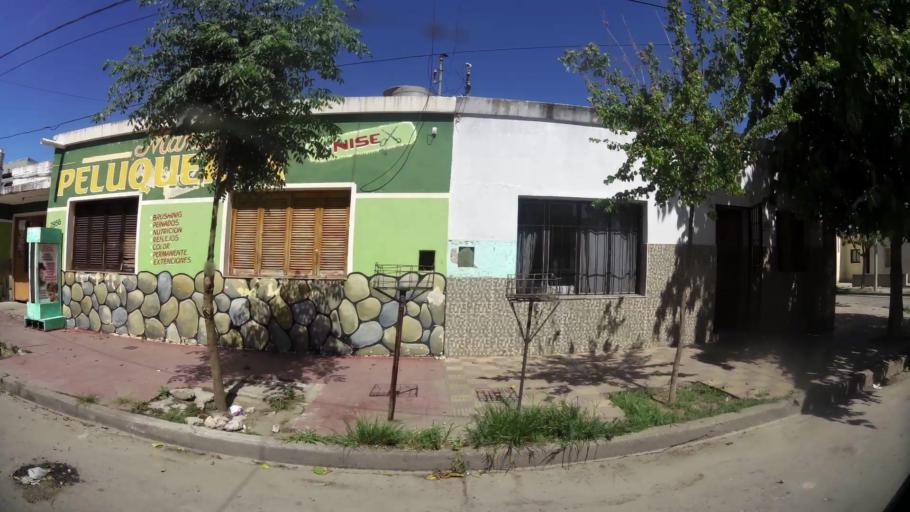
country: AR
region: Cordoba
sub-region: Departamento de Capital
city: Cordoba
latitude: -31.3744
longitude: -64.1543
